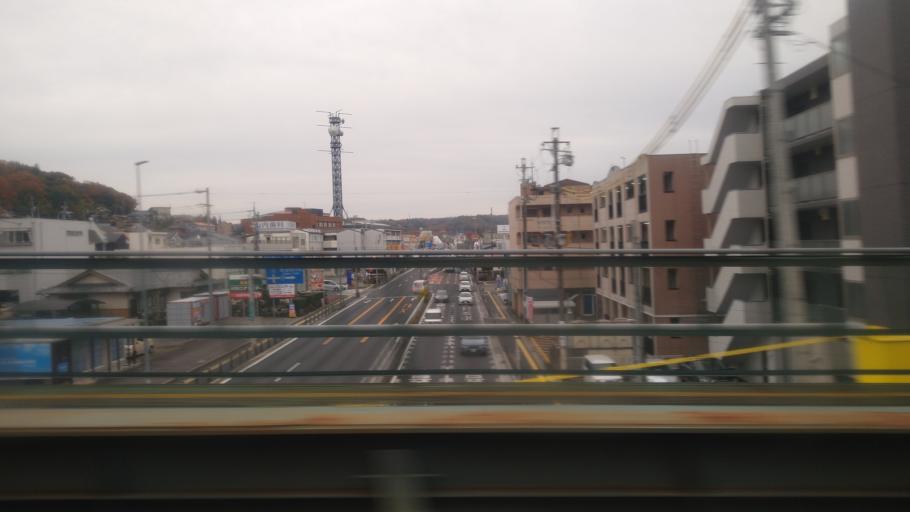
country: JP
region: Gifu
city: Tajimi
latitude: 35.3411
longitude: 137.1274
